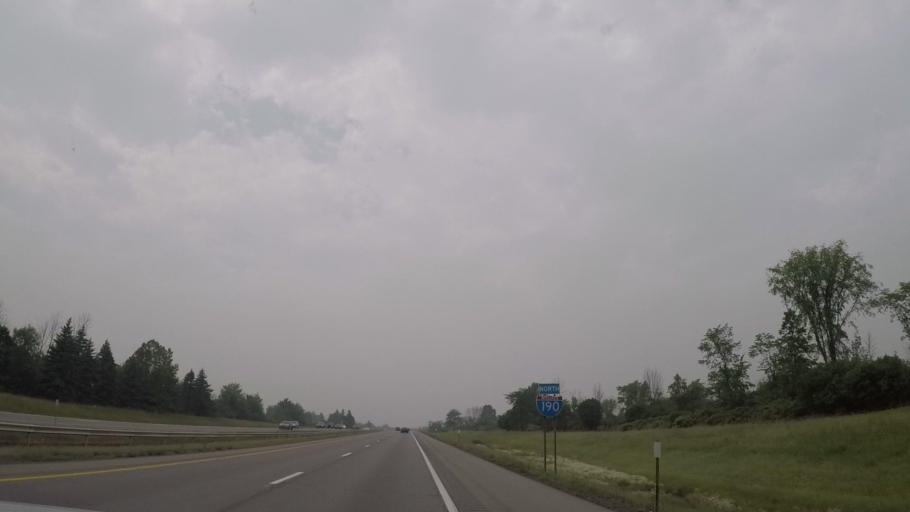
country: US
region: New York
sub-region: Erie County
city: Grandyle Village
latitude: 43.0289
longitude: -78.9792
